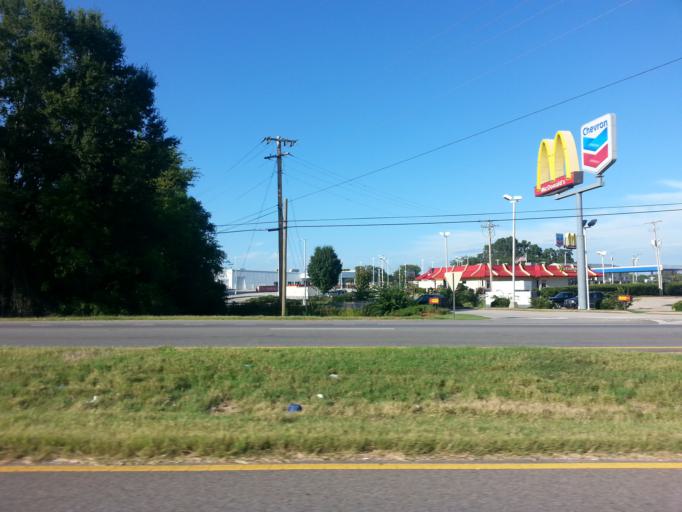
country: US
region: Alabama
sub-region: Colbert County
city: Muscle Shoals
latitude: 34.7120
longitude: -87.6697
